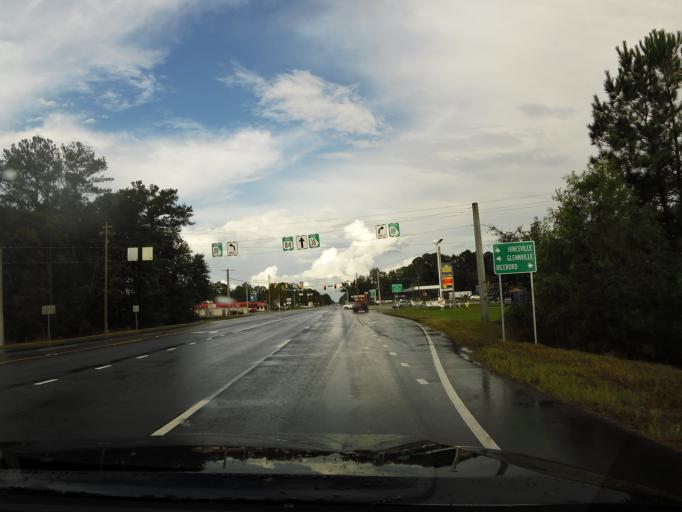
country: US
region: Georgia
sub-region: Liberty County
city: Walthourville
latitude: 31.7727
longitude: -81.6348
